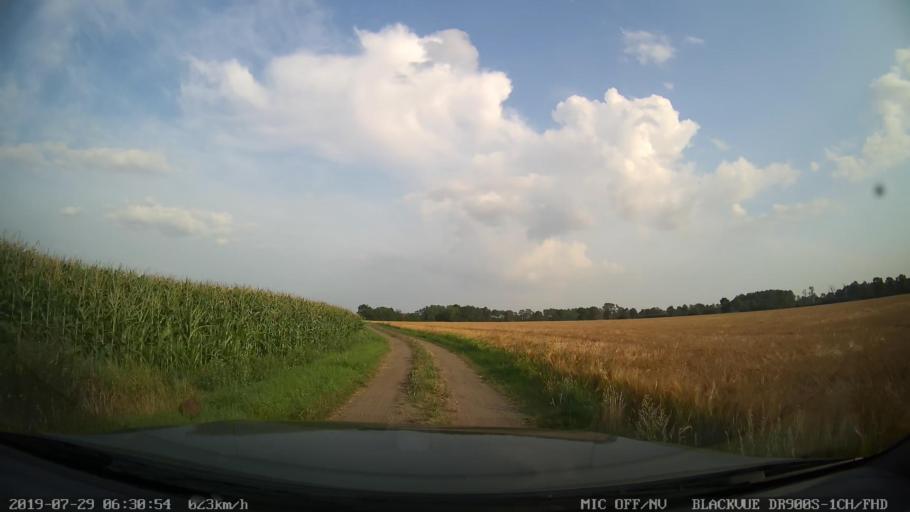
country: SE
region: Skane
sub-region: Helsingborg
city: Odakra
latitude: 56.1246
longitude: 12.7371
